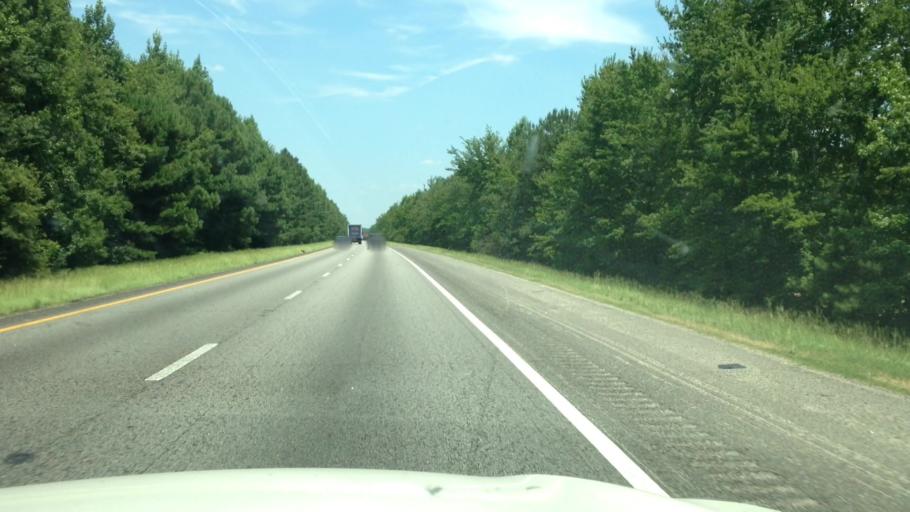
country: US
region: South Carolina
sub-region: Dillon County
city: Latta
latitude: 34.3212
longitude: -79.5841
